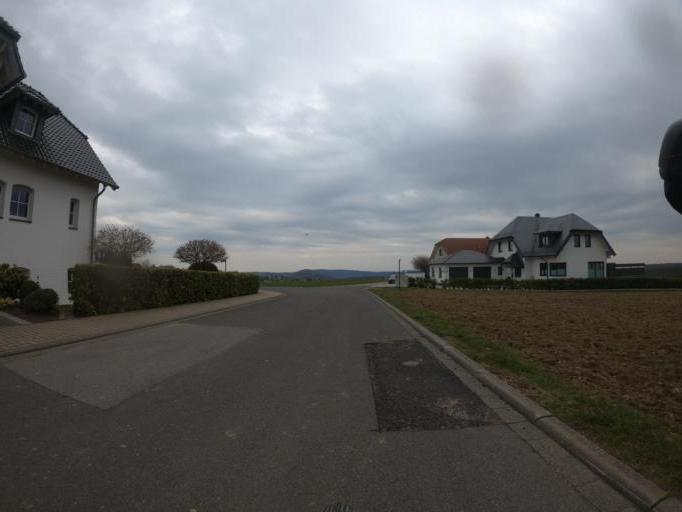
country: DE
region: North Rhine-Westphalia
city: Heimbach
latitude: 50.6610
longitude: 6.4161
